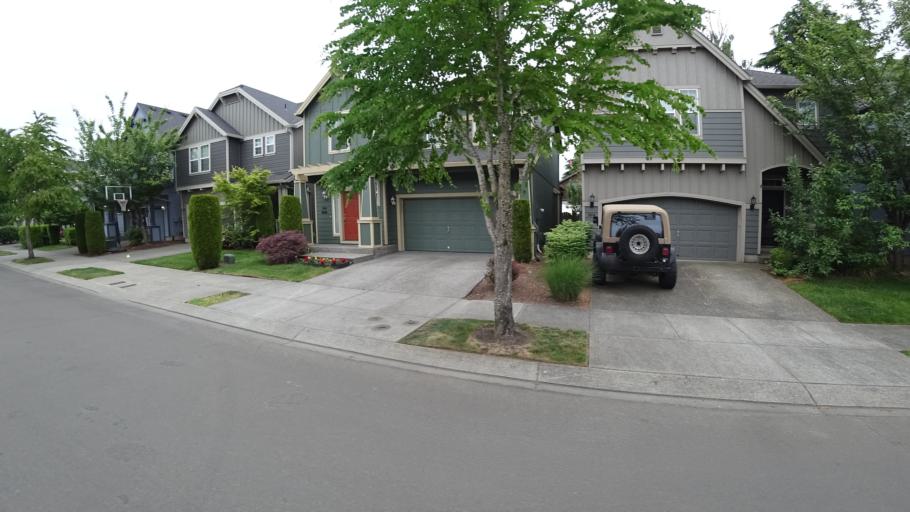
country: US
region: Oregon
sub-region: Washington County
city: Hillsboro
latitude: 45.4940
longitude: -122.9679
